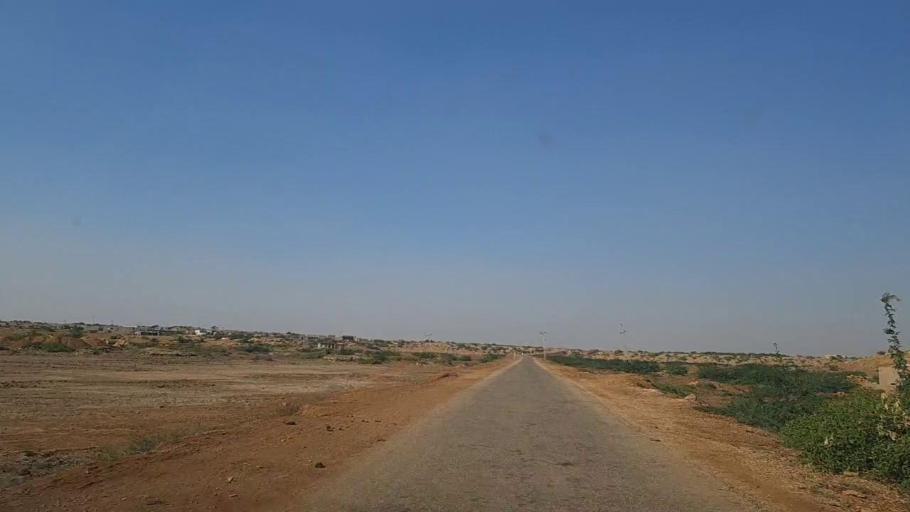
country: PK
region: Sindh
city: Daro Mehar
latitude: 24.9900
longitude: 68.1321
